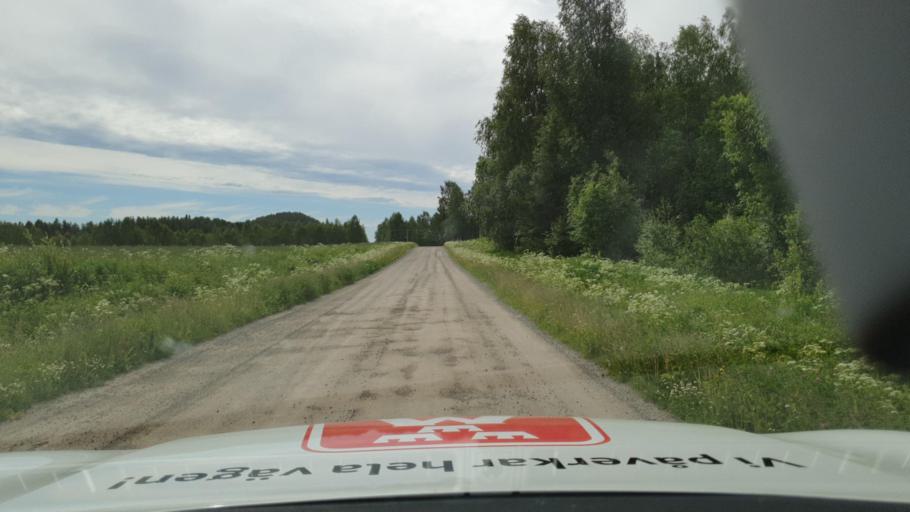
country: SE
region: Vaesterbotten
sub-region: Robertsfors Kommun
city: Robertsfors
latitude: 64.2637
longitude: 20.6423
